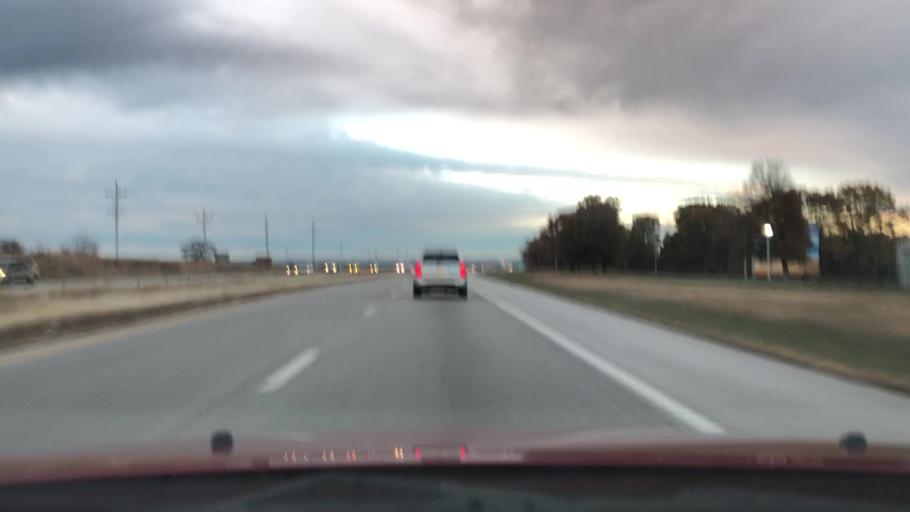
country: US
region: Missouri
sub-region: Christian County
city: Ozark
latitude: 37.0509
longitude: -93.2267
